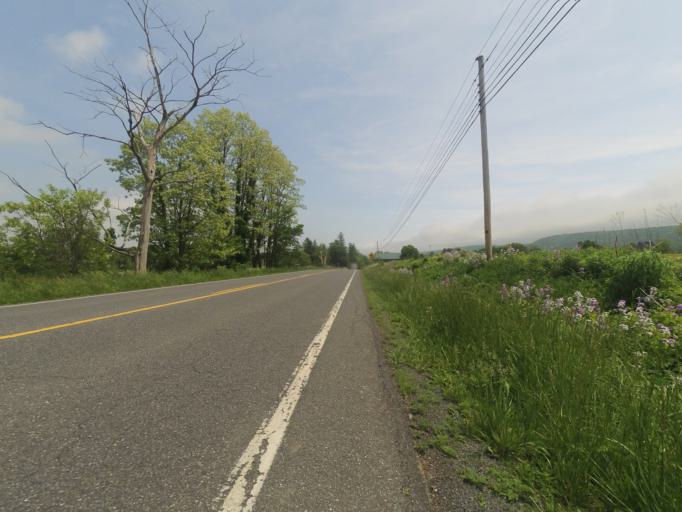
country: US
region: Pennsylvania
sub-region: Centre County
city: Stormstown
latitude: 40.7039
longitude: -77.9845
